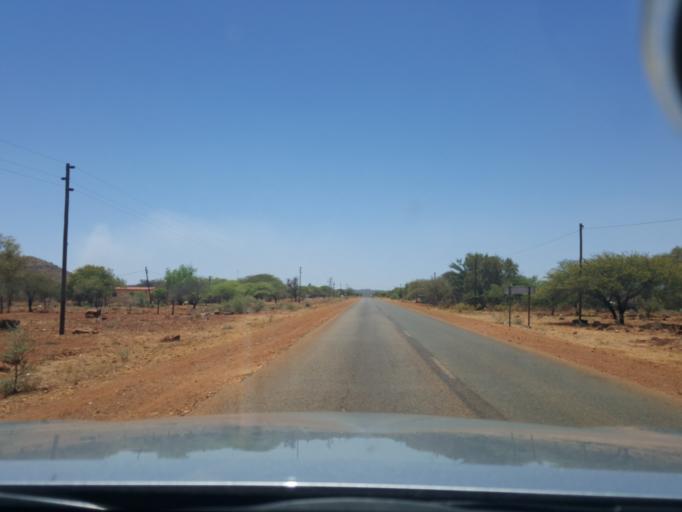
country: ZA
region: North-West
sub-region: Ngaka Modiri Molema District Municipality
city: Zeerust
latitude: -25.4169
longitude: 25.9518
